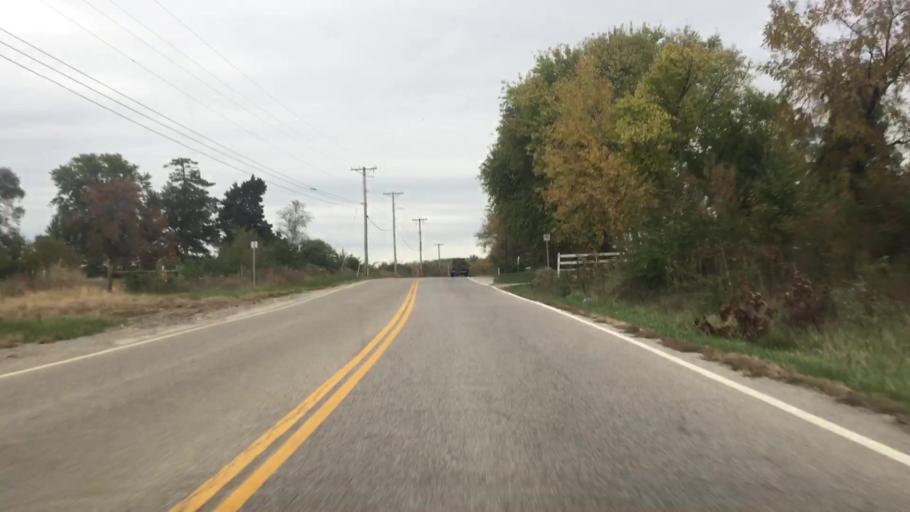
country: US
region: Missouri
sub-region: Jackson County
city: Lees Summit
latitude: 38.8886
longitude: -94.3593
